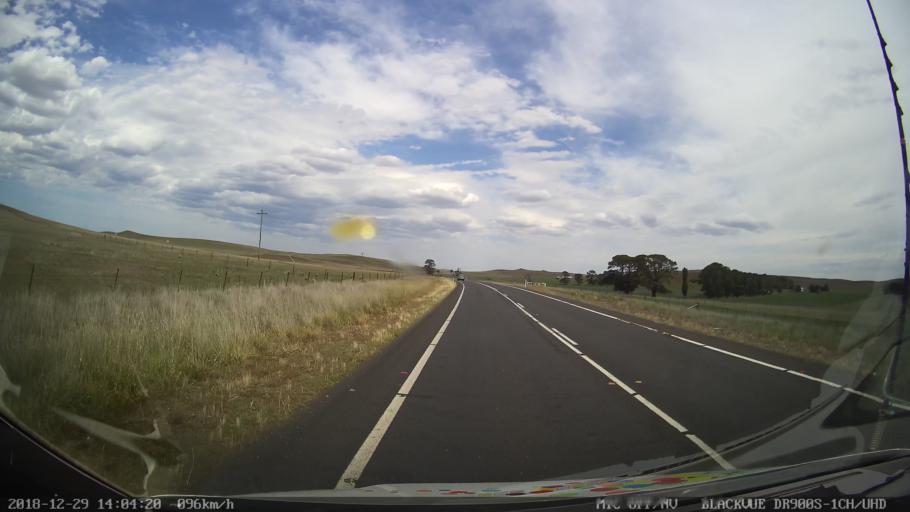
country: AU
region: New South Wales
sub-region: Cooma-Monaro
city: Cooma
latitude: -36.3146
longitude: 149.1863
